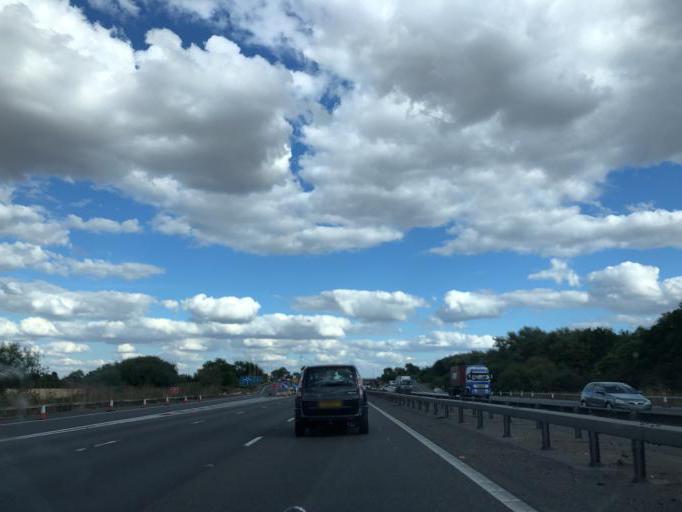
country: GB
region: England
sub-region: Milton Keynes
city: Broughton
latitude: 52.0614
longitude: -0.7063
